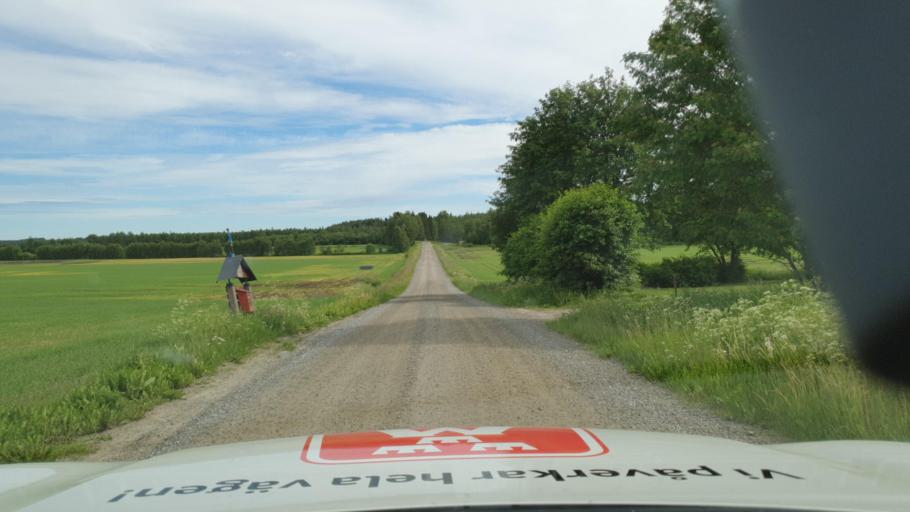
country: SE
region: Vaesterbotten
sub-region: Robertsfors Kommun
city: Robertsfors
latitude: 64.3901
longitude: 21.0310
